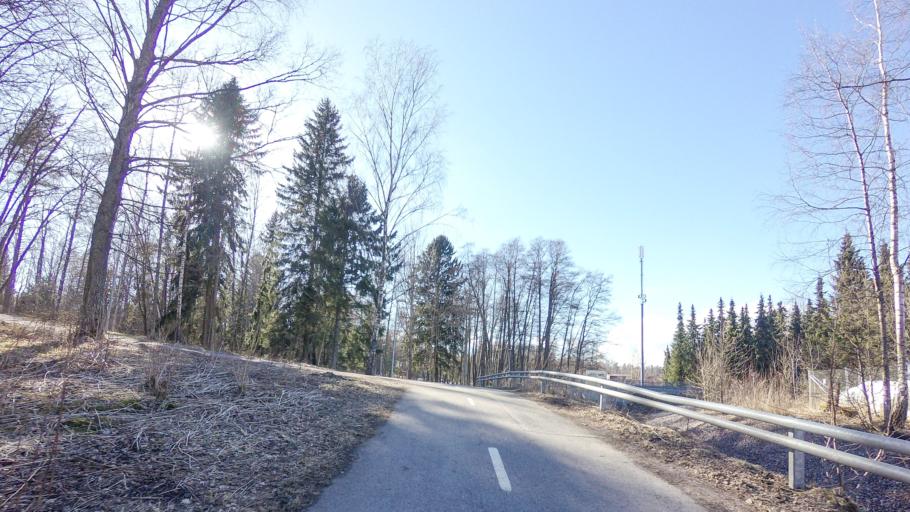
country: FI
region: Uusimaa
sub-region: Helsinki
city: Helsinki
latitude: 60.1660
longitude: 25.0567
